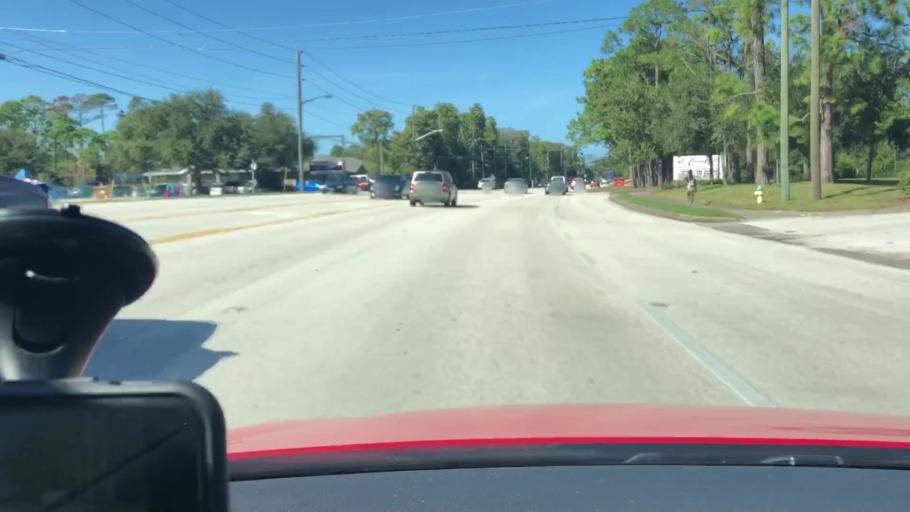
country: US
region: Florida
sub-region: Volusia County
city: South Daytona
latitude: 29.1573
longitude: -81.0385
